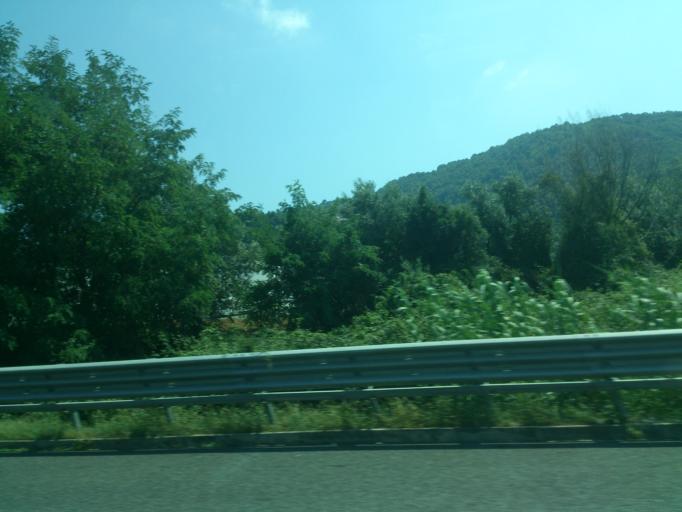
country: IT
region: Calabria
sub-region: Provincia di Vibo-Valentia
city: Francavilla Angitola
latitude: 38.8009
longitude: 16.2294
